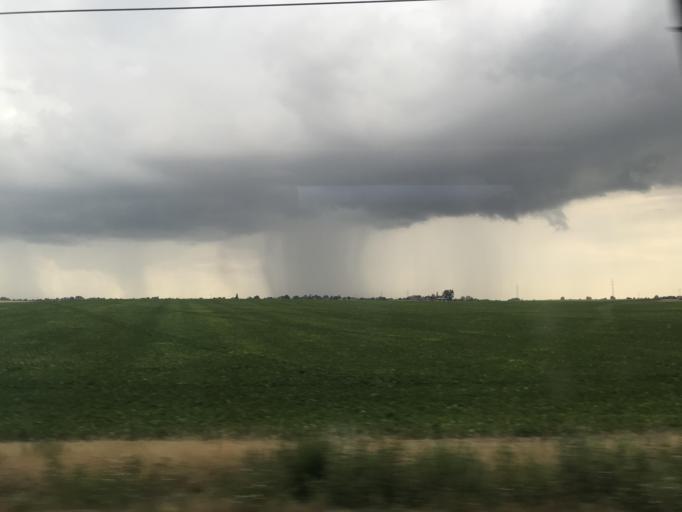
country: BE
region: Wallonia
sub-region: Province de Liege
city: Fexhe-le-Haut-Clocher
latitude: 50.6792
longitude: 5.4206
